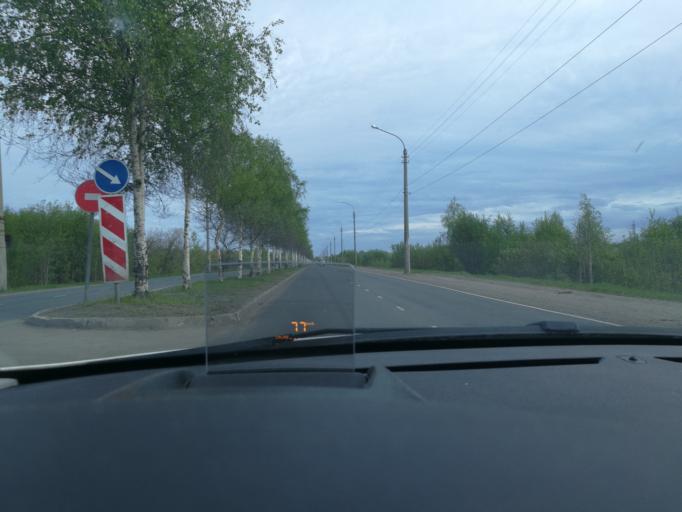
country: RU
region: Arkhangelskaya
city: Arkhangel'sk
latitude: 64.6007
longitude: 40.5252
